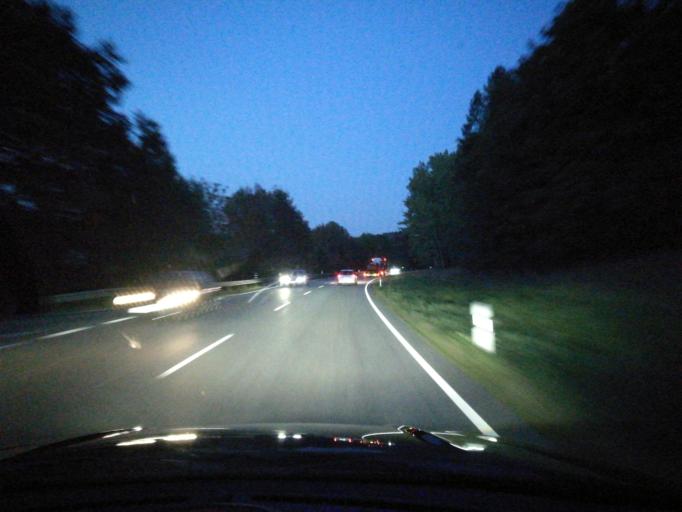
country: DE
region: Bavaria
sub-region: Lower Bavaria
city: Bad Abbach
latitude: 48.9610
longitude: 12.0500
